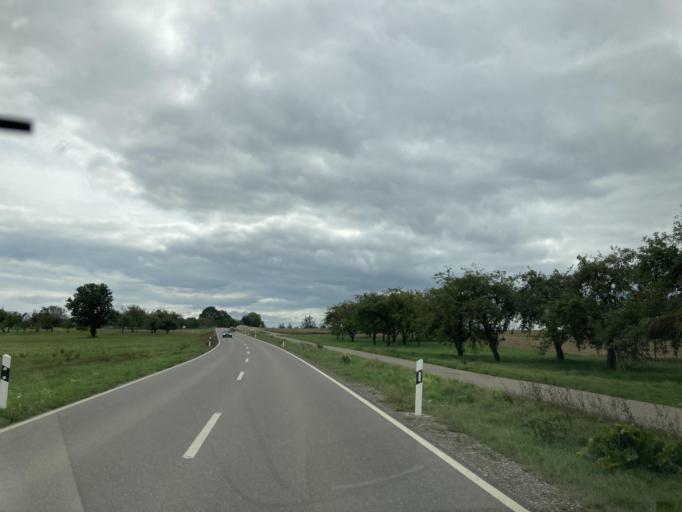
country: DE
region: Baden-Wuerttemberg
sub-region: Regierungsbezirk Stuttgart
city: Bondorf
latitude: 48.5237
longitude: 8.8163
